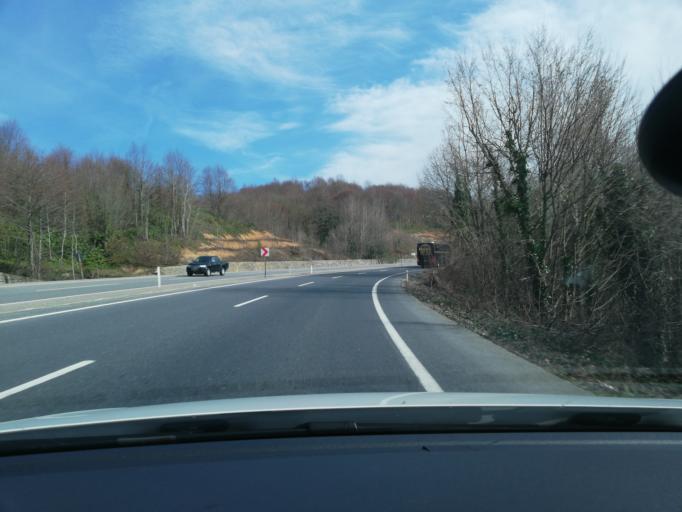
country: TR
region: Zonguldak
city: Ormanli
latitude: 41.3330
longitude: 31.5967
